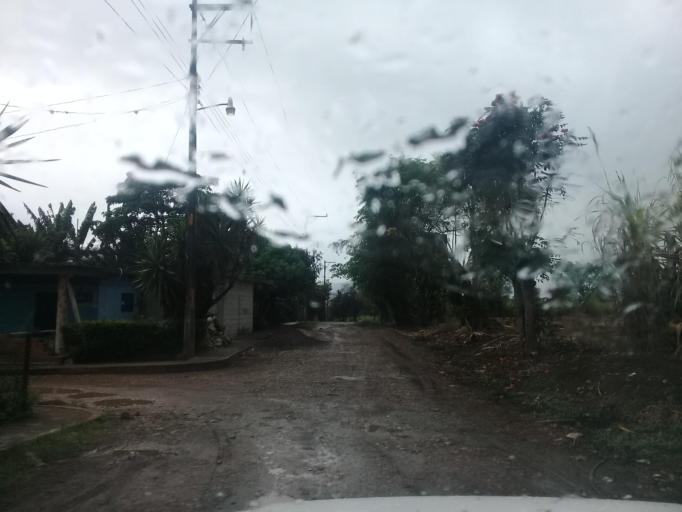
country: MX
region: Veracruz
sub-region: Amatlan de los Reyes
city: Trapiche Viejo
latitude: 18.8434
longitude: -96.9474
